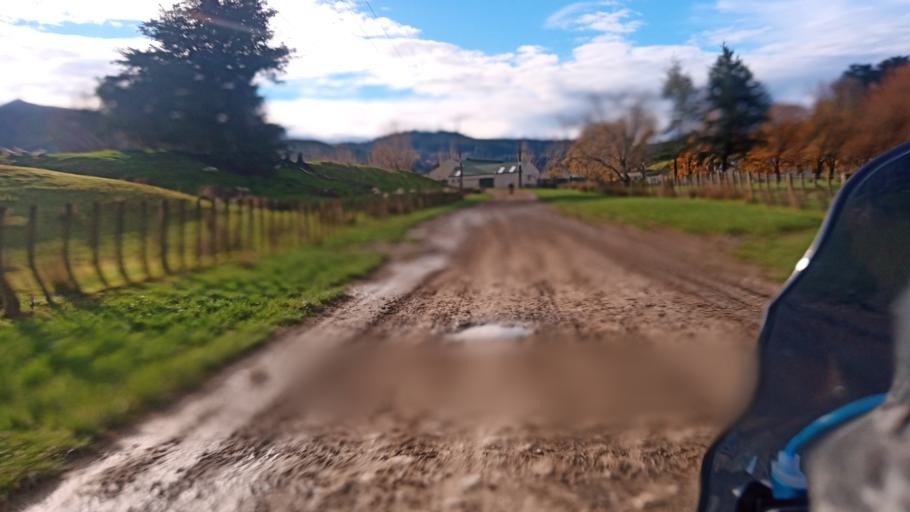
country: NZ
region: Gisborne
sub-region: Gisborne District
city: Gisborne
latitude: -38.3501
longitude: 177.9393
